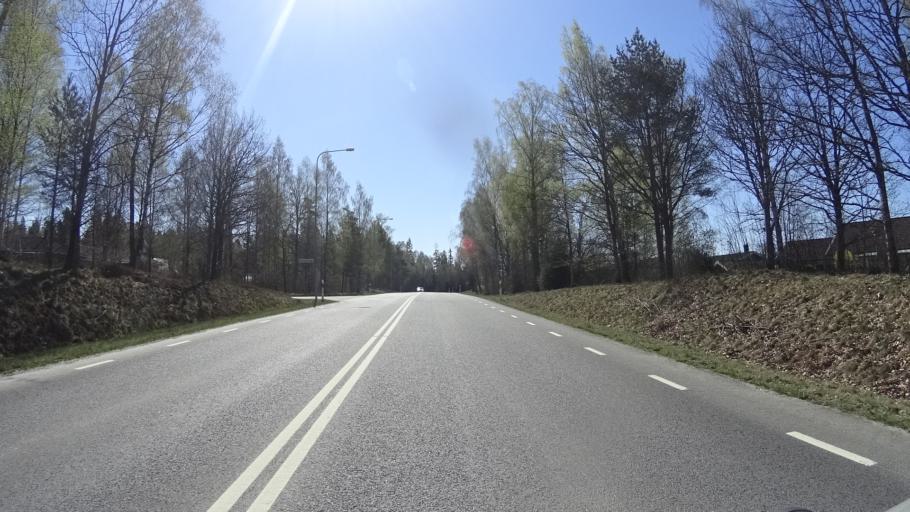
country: SE
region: Kronoberg
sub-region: Ljungby Kommun
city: Ljungby
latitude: 56.8337
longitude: 13.9729
